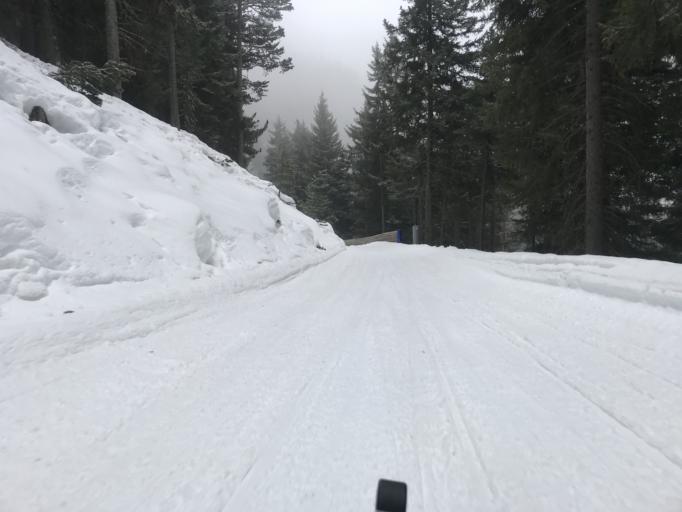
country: IT
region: Trentino-Alto Adige
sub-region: Bolzano
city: San Pietro
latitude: 46.6879
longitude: 11.6996
